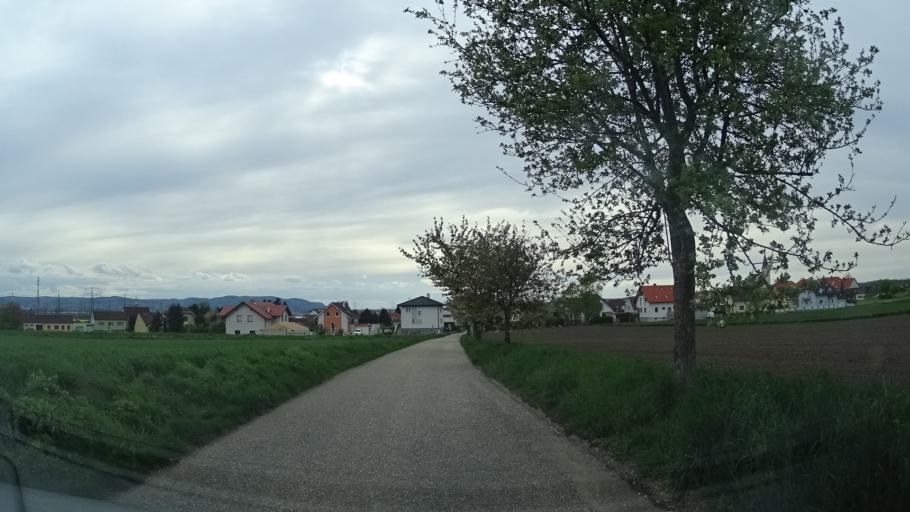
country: AT
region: Lower Austria
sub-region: Politischer Bezirk Korneuburg
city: Stetten
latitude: 48.3649
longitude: 16.3901
